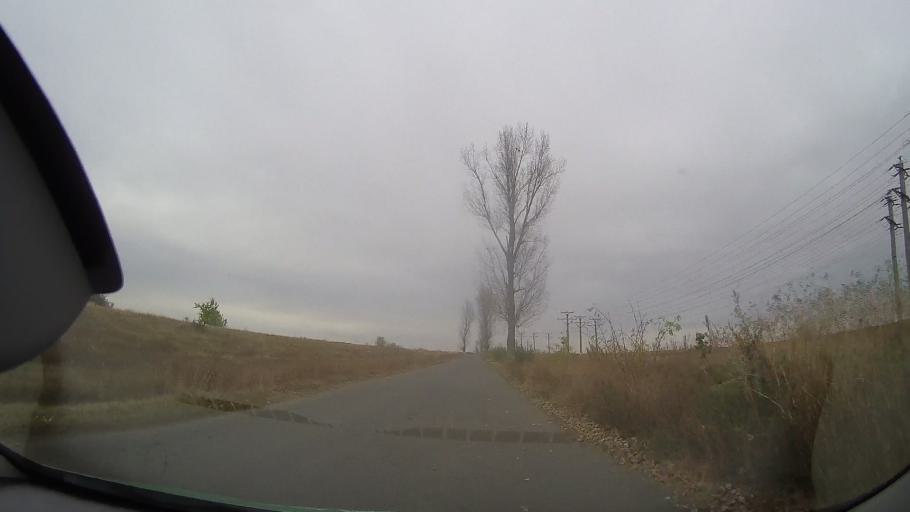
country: RO
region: Braila
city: Dudesti
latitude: 44.8991
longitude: 27.4327
